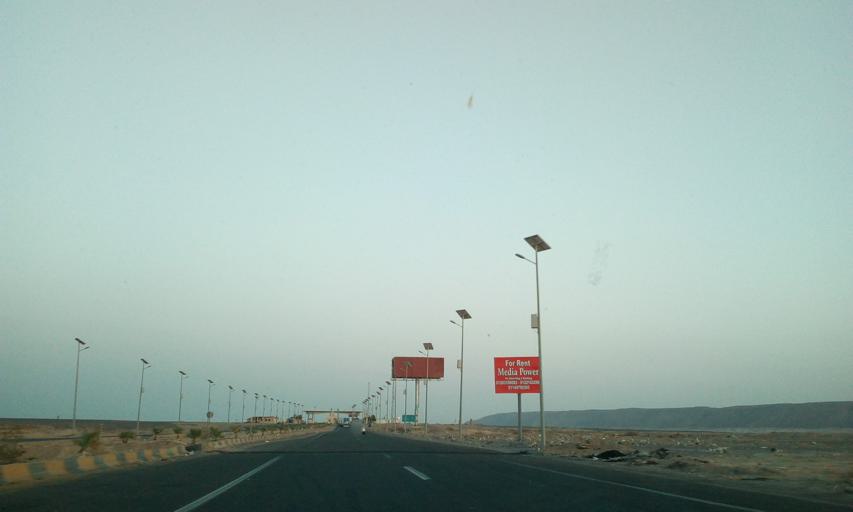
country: EG
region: Red Sea
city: El Gouna
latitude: 27.4244
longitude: 33.6128
